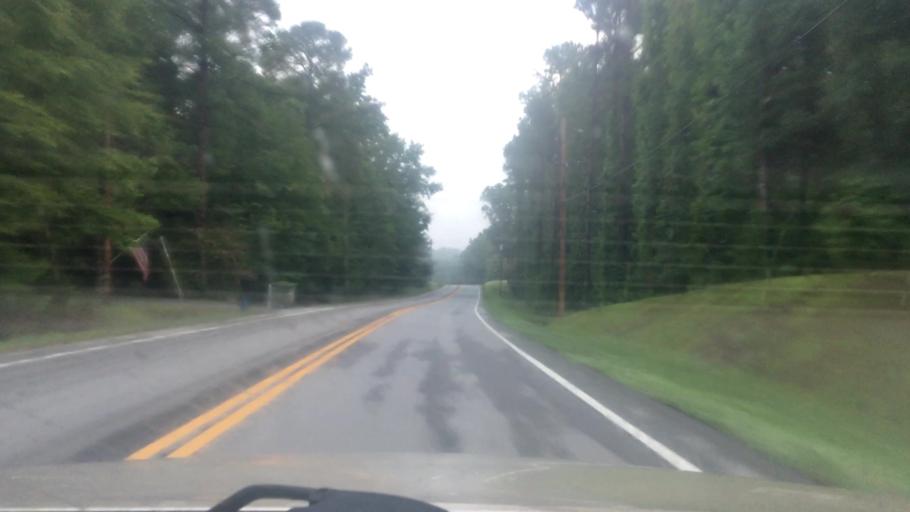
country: US
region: South Carolina
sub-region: Lexington County
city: Irmo
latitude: 34.1430
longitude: -81.1912
